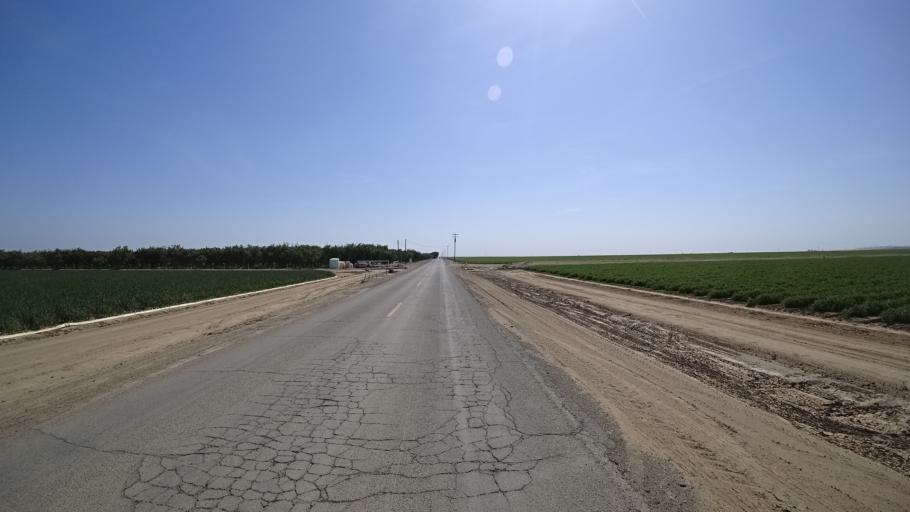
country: US
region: California
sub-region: Kings County
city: Kettleman City
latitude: 36.0725
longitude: -120.0405
